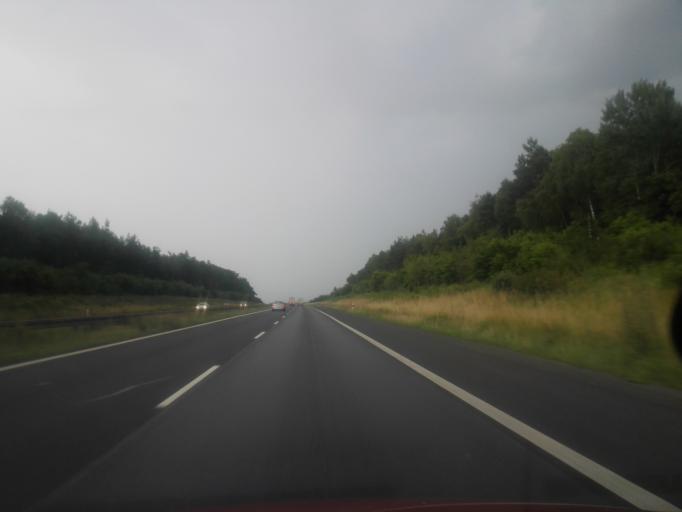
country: PL
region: Silesian Voivodeship
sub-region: Powiat czestochowski
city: Borowno
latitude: 50.9822
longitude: 19.2788
